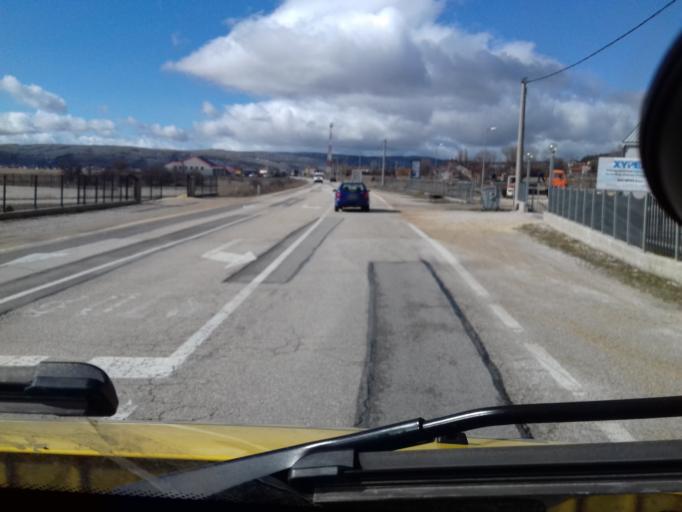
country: BA
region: Federation of Bosnia and Herzegovina
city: Tomislavgrad
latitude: 43.7062
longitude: 17.2277
